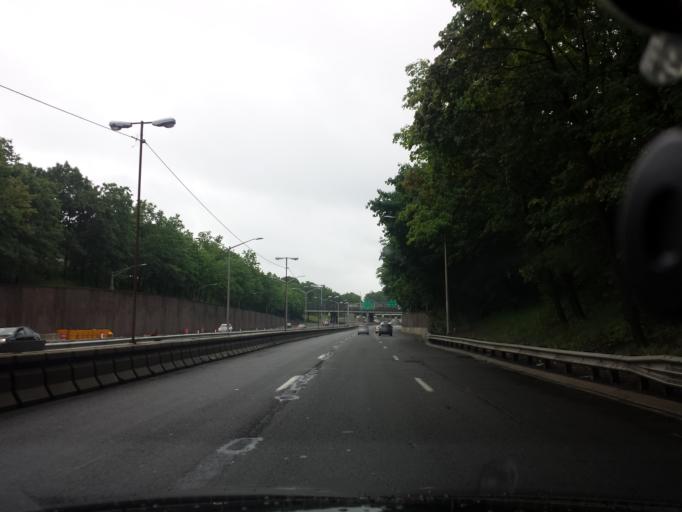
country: US
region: New York
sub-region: Kings County
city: Bensonhurst
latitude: 40.6268
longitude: -74.0184
